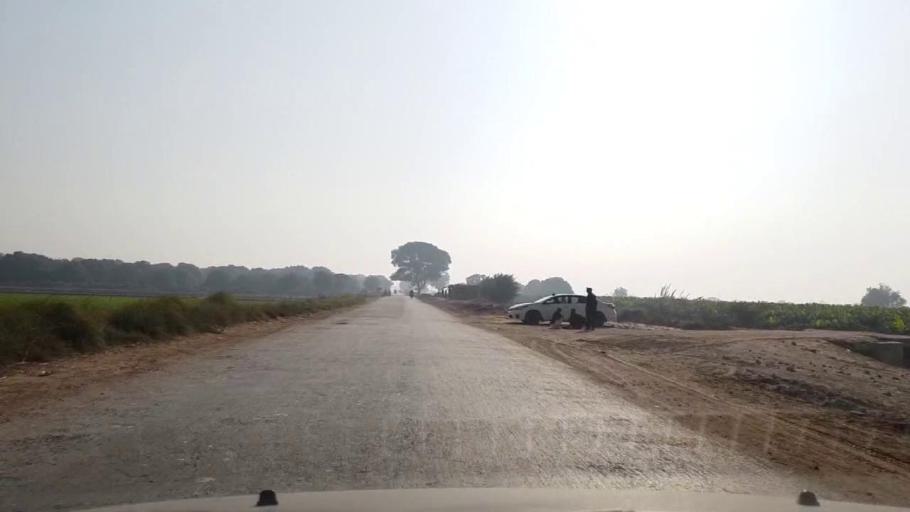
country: PK
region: Sindh
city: Matiari
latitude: 25.5913
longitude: 68.4747
